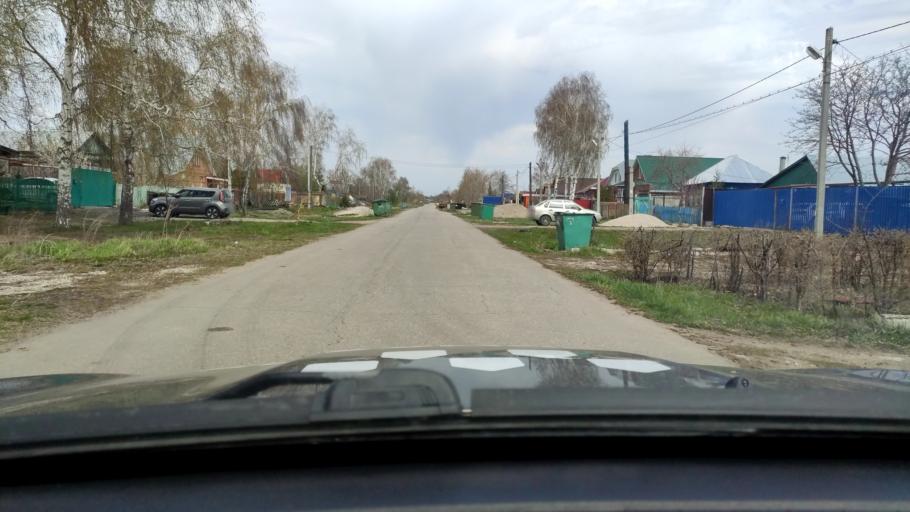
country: RU
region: Samara
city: Tol'yatti
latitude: 53.5584
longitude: 49.3982
